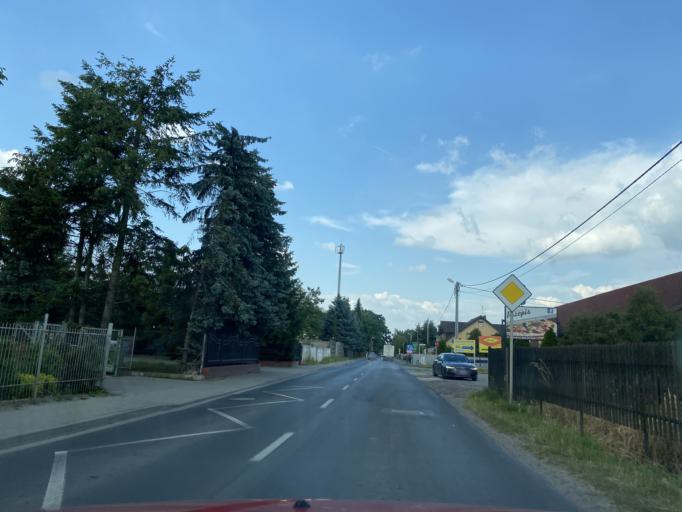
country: PL
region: Greater Poland Voivodeship
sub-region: Powiat poznanski
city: Dopiewo
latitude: 52.3722
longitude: 16.7380
